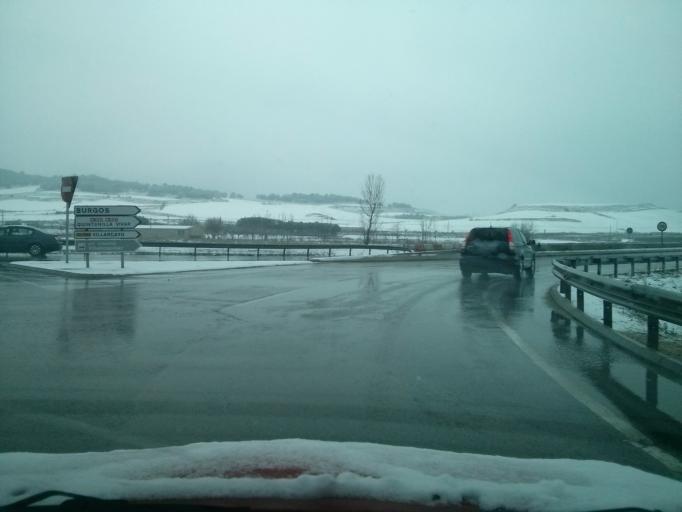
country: ES
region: Castille and Leon
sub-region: Provincia de Burgos
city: Sotragero
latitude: 42.3850
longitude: -3.6956
